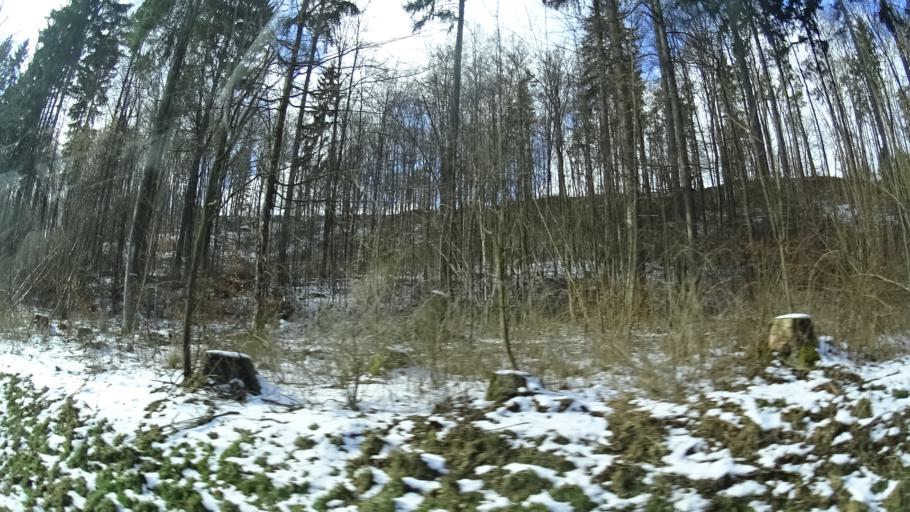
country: DE
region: Thuringia
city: Kuhndorf
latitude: 50.5906
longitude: 10.4640
